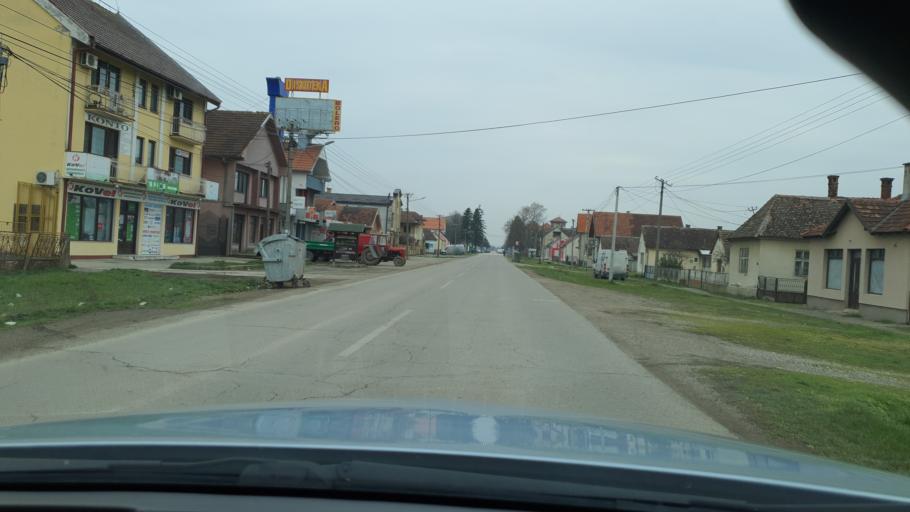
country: RS
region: Central Serbia
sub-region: Macvanski Okrug
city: Bogatic
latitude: 44.8341
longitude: 19.4848
